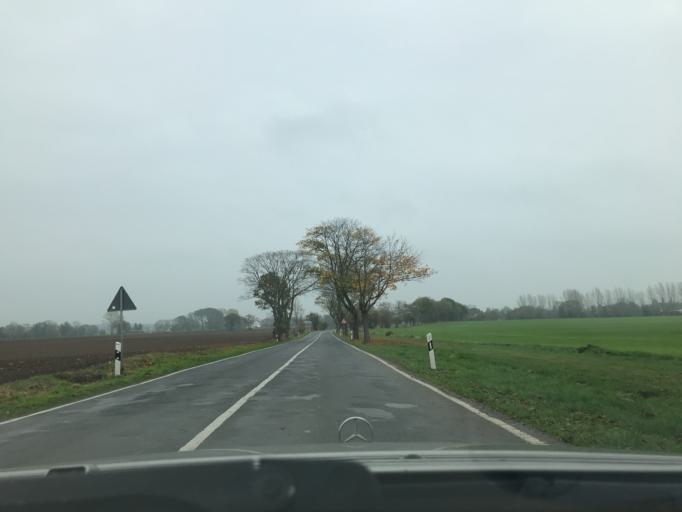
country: DE
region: Mecklenburg-Vorpommern
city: Kroslin
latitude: 54.1011
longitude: 13.6863
